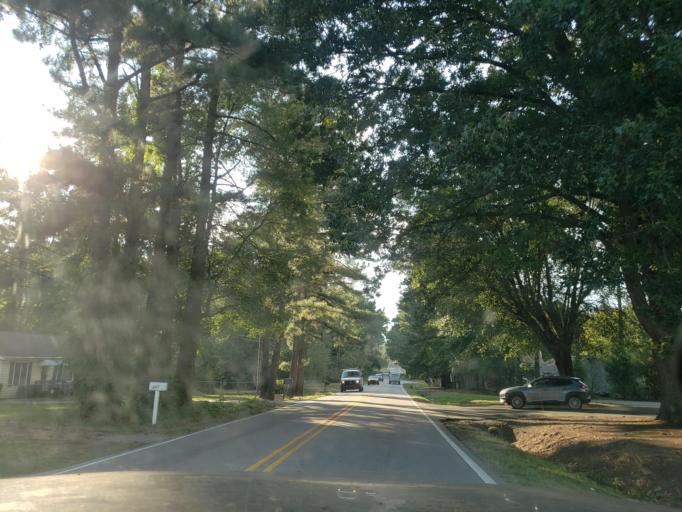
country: US
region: North Carolina
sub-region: Durham County
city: Durham
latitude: 35.9671
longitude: -78.9222
